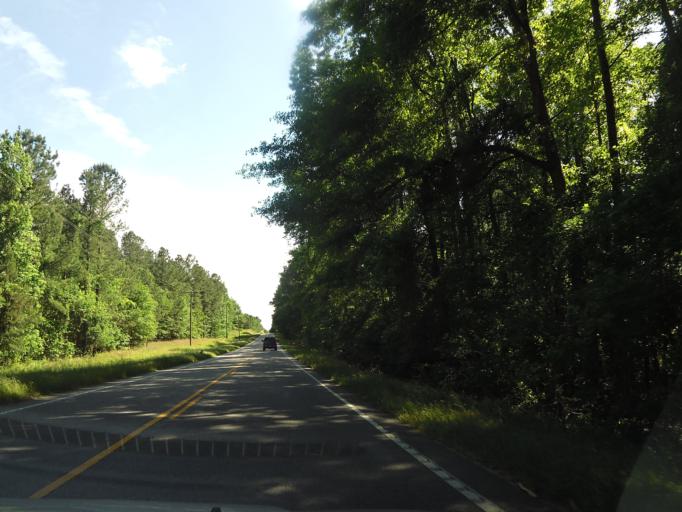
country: US
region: South Carolina
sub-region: Bamberg County
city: Denmark
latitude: 33.2814
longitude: -81.1509
